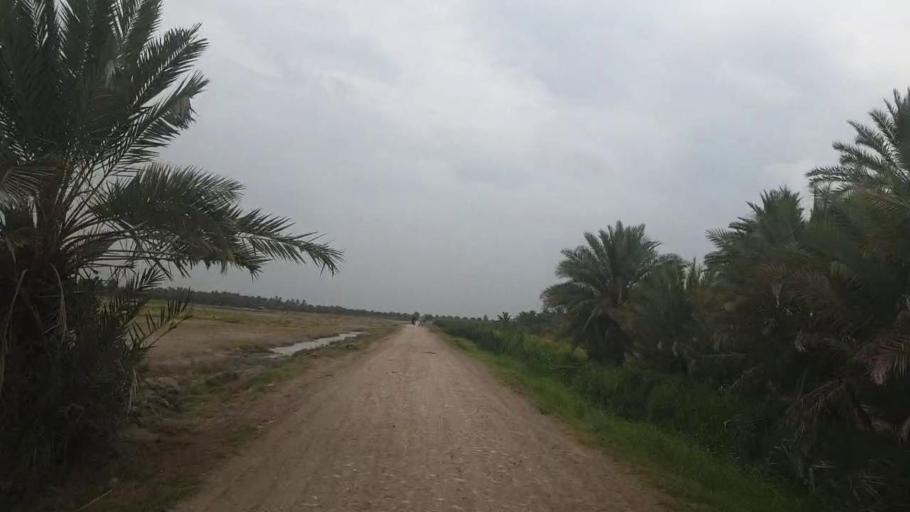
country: PK
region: Sindh
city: Khairpur
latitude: 27.5622
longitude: 68.7121
